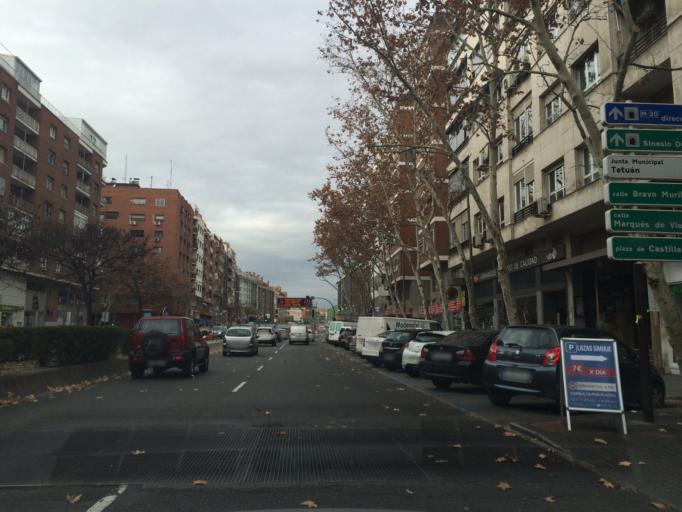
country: ES
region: Madrid
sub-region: Provincia de Madrid
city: Chamartin
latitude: 40.4598
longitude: -3.6955
